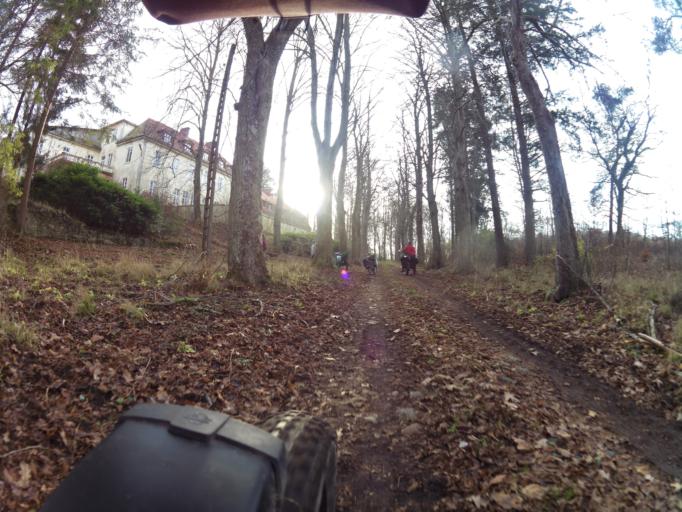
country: PL
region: West Pomeranian Voivodeship
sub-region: Powiat koszalinski
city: Polanow
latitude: 54.0792
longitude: 16.6647
